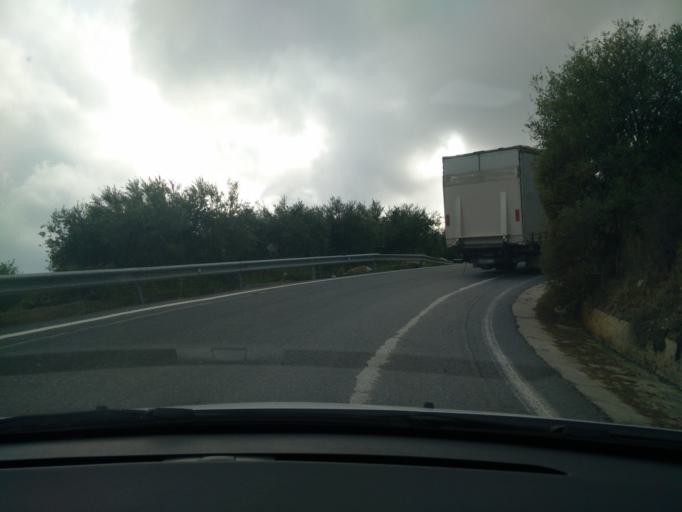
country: GR
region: Crete
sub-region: Nomos Lasithiou
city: Gra Liyia
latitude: 35.0242
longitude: 25.5629
